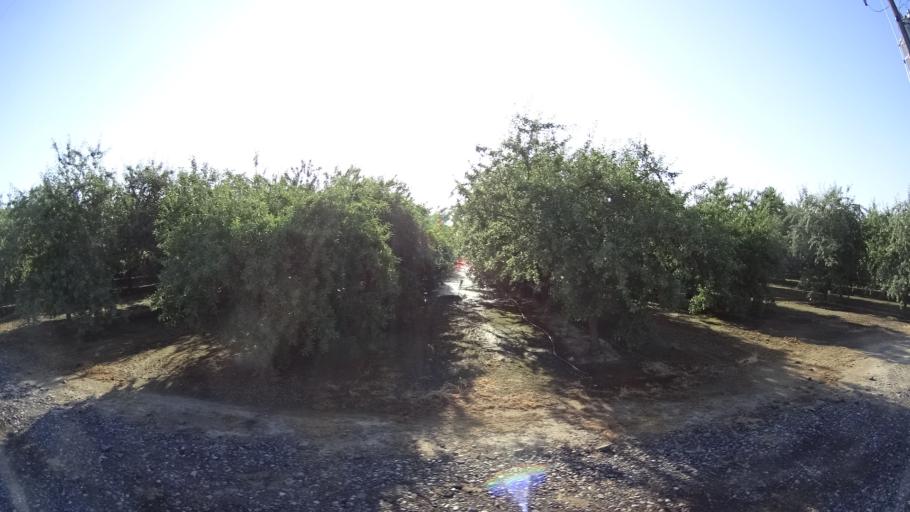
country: US
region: California
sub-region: Kings County
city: Lemoore
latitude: 36.2886
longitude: -119.7447
